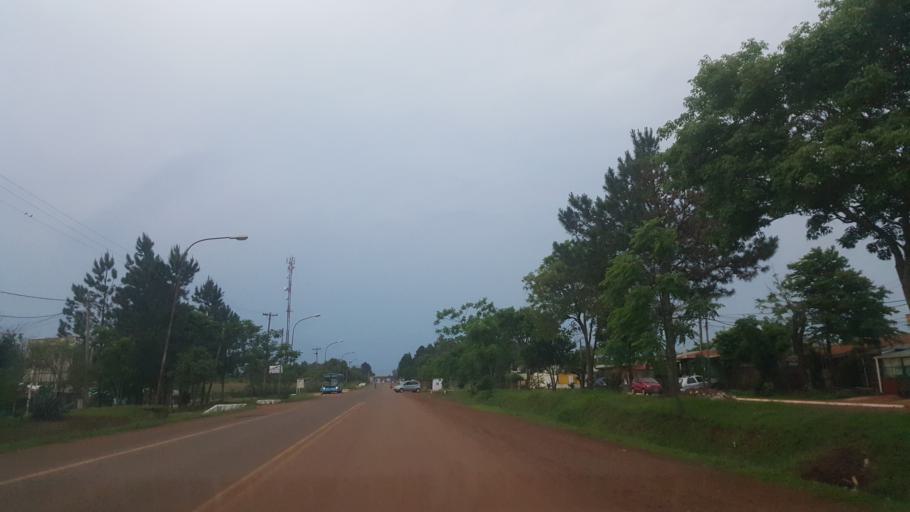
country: AR
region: Misiones
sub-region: Departamento de Candelaria
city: Candelaria
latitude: -27.4784
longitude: -55.7468
